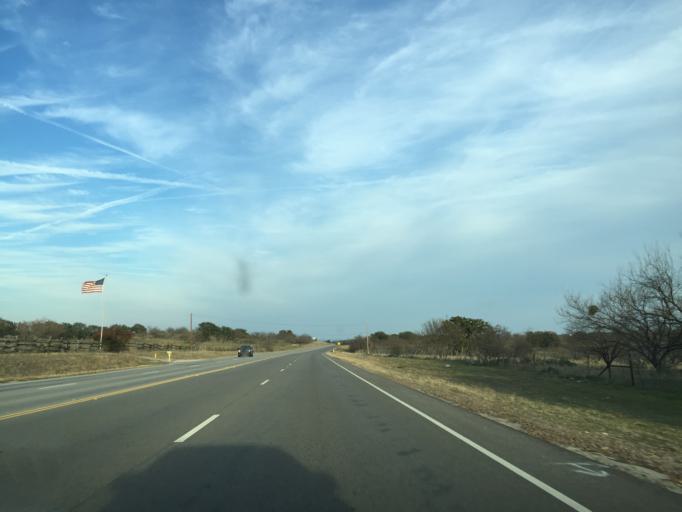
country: US
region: Texas
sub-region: Llano County
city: Llano
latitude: 30.7609
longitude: -98.6554
